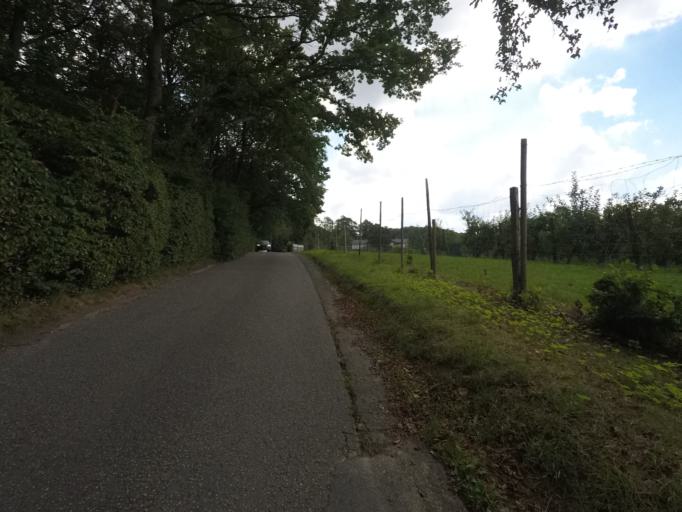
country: DE
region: North Rhine-Westphalia
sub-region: Regierungsbezirk Detmold
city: Bielefeld
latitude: 52.0309
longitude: 8.4760
